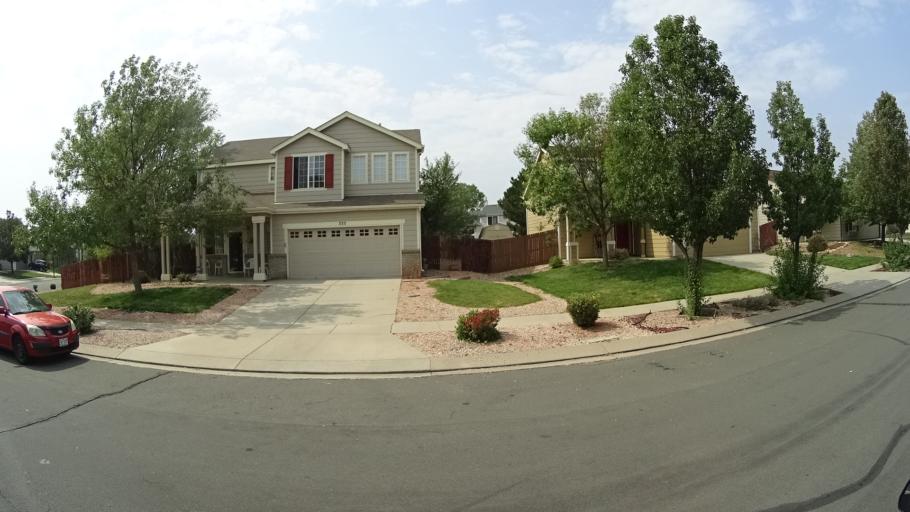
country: US
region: Colorado
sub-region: El Paso County
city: Cimarron Hills
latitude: 38.8238
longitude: -104.7322
